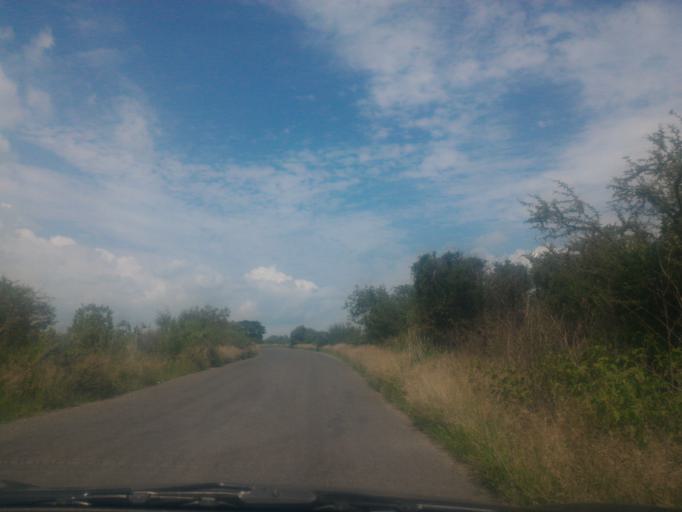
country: MX
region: Guanajuato
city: Ciudad Manuel Doblado
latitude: 20.8341
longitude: -102.0128
